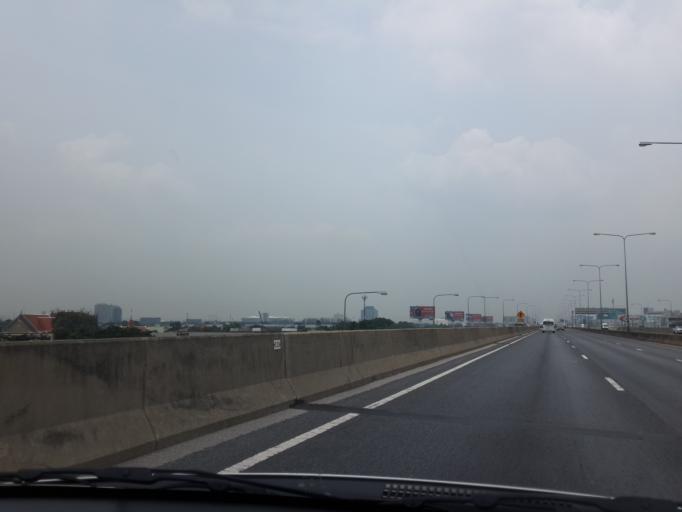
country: TH
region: Bangkok
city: Chatuchak
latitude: 13.8514
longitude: 100.5635
